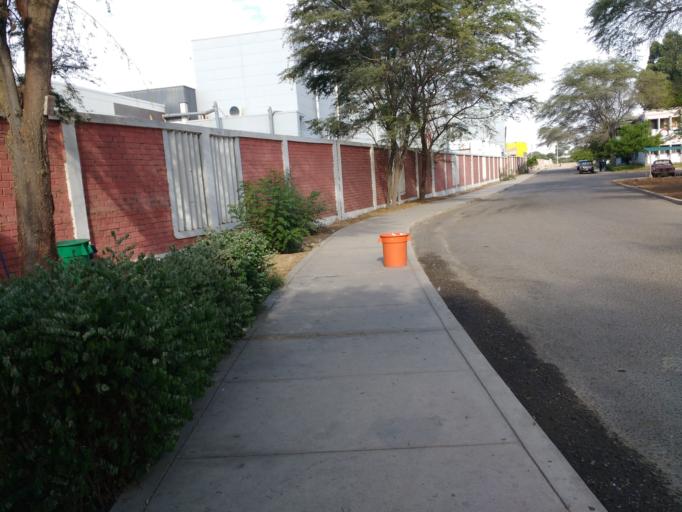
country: PE
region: Piura
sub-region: Provincia de Piura
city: Piura
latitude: -5.1818
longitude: -80.6209
